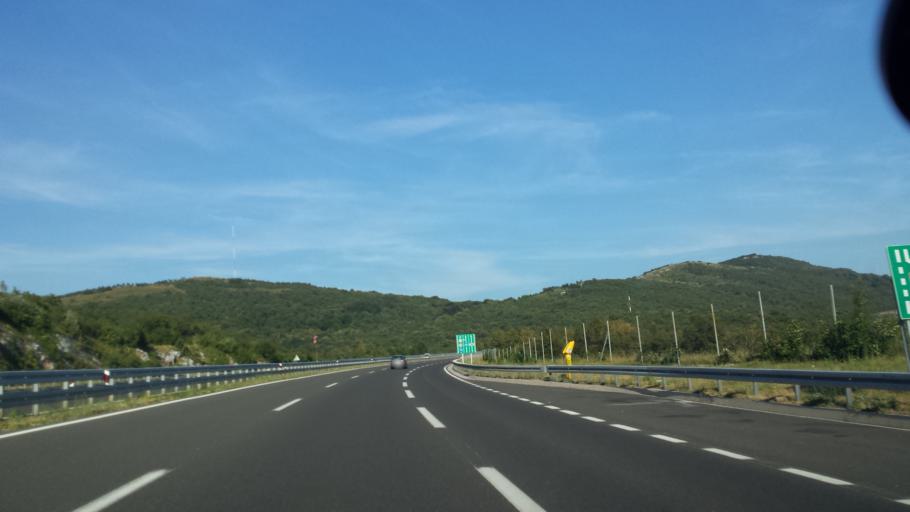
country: HR
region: Primorsko-Goranska
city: Krasica
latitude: 45.3623
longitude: 14.5676
